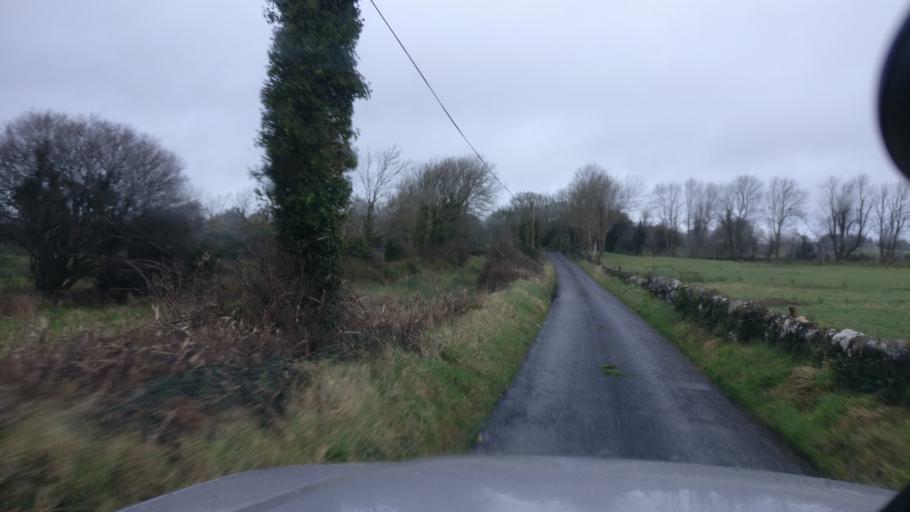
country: IE
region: Connaught
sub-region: County Galway
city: Loughrea
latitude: 53.1780
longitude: -8.6089
